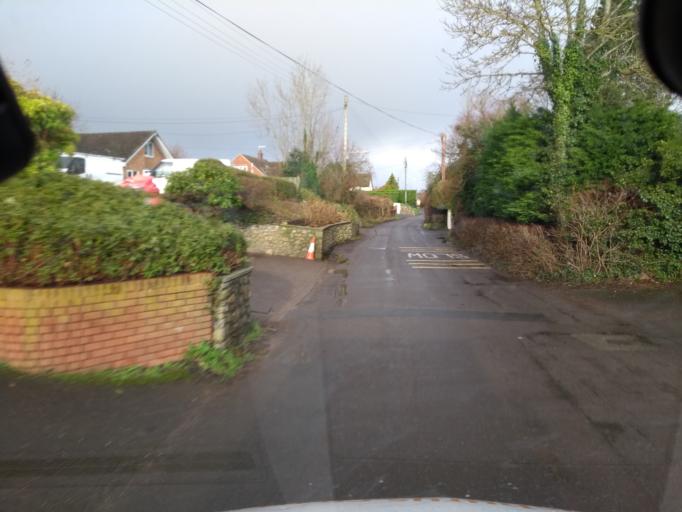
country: GB
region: England
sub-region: Somerset
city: Creech Saint Michael
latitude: 51.0166
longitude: -3.0496
